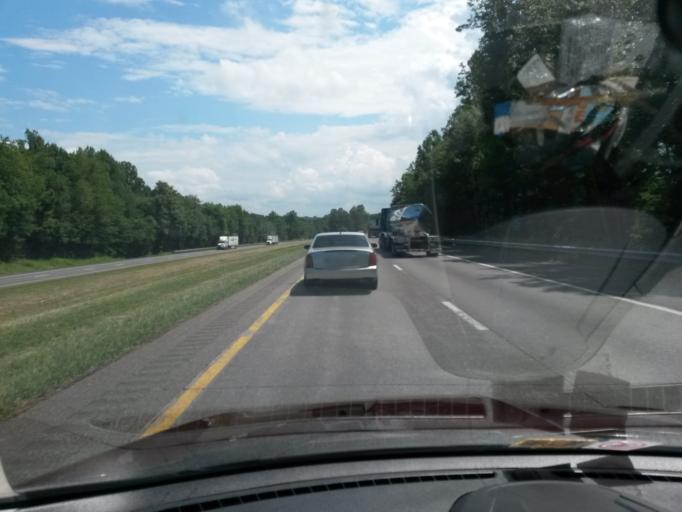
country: US
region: North Carolina
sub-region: Surry County
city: Dobson
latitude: 36.3809
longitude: -80.7901
